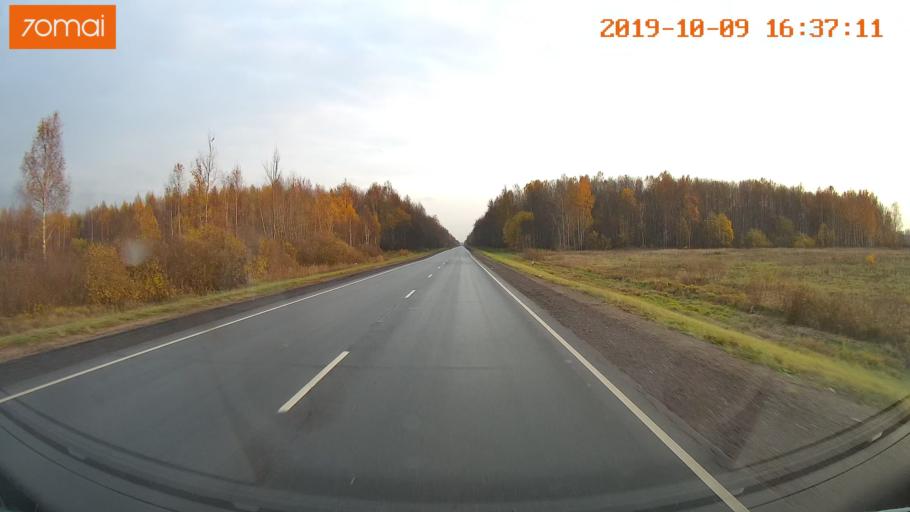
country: RU
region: Kostroma
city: Volgorechensk
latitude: 57.5306
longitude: 41.0216
